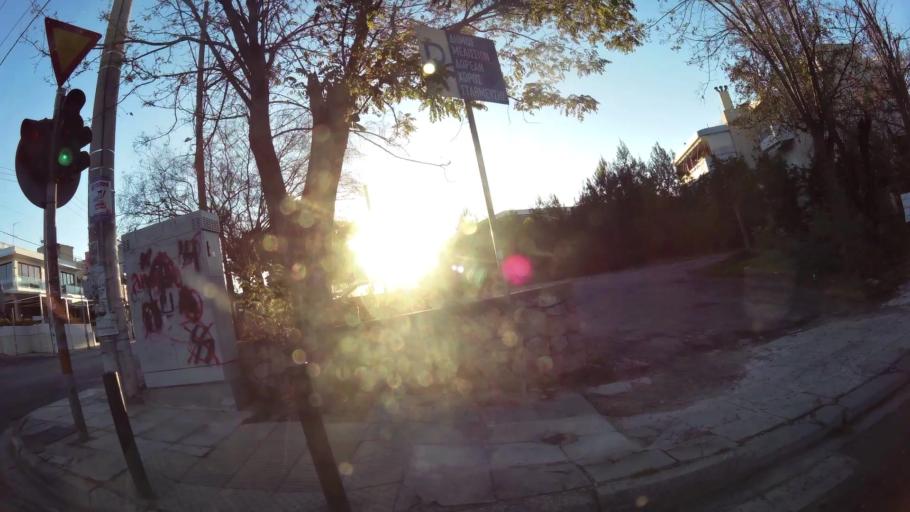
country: GR
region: Attica
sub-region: Nomarchia Athinas
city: Melissia
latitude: 38.0511
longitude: 23.8318
